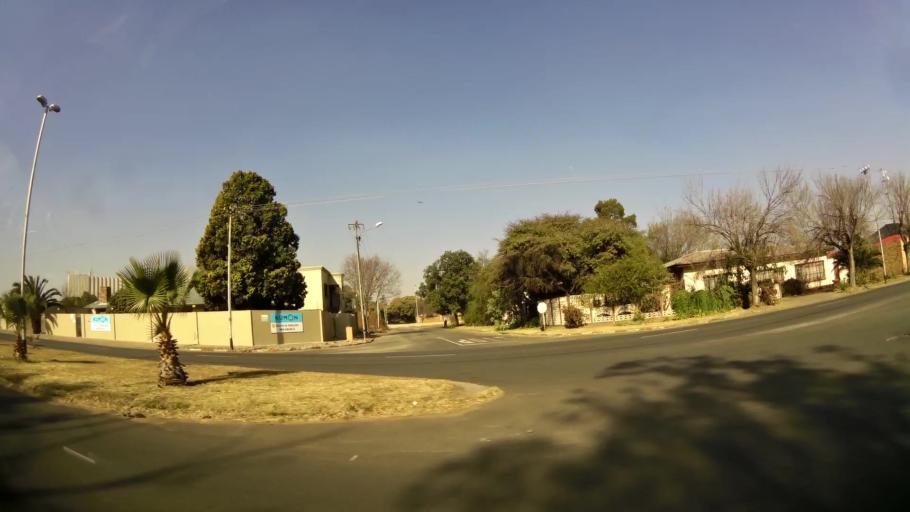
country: ZA
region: Gauteng
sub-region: West Rand District Municipality
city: Randfontein
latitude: -26.1667
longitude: 27.7056
